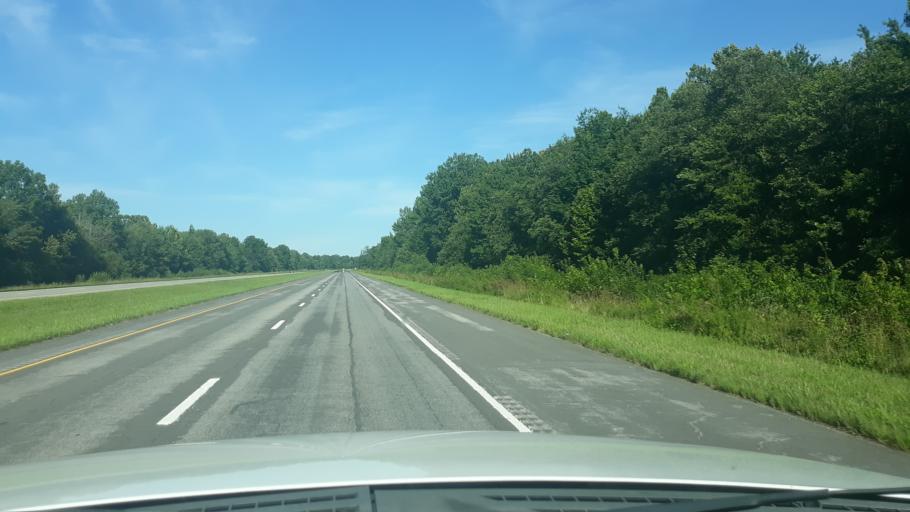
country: US
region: Illinois
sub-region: Saline County
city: Carrier Mills
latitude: 37.7343
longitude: -88.6851
